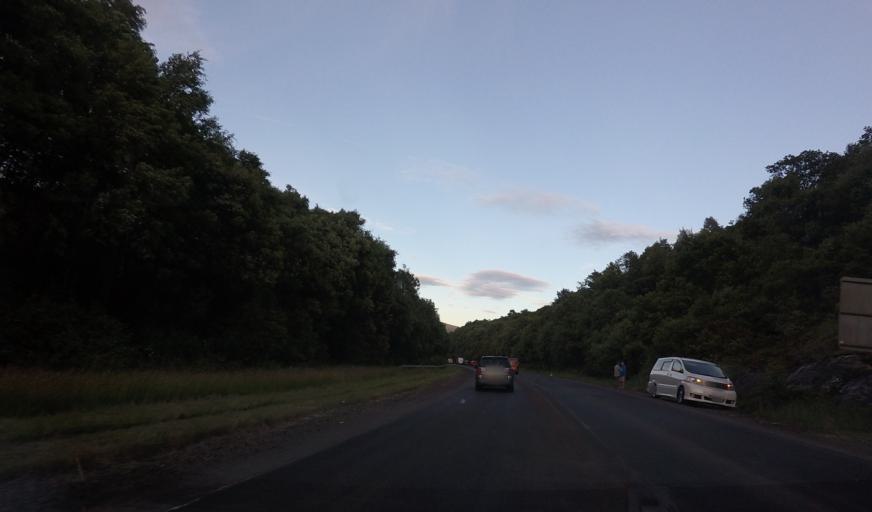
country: GB
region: Scotland
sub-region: Argyll and Bute
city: Helensburgh
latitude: 56.1686
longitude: -4.6756
